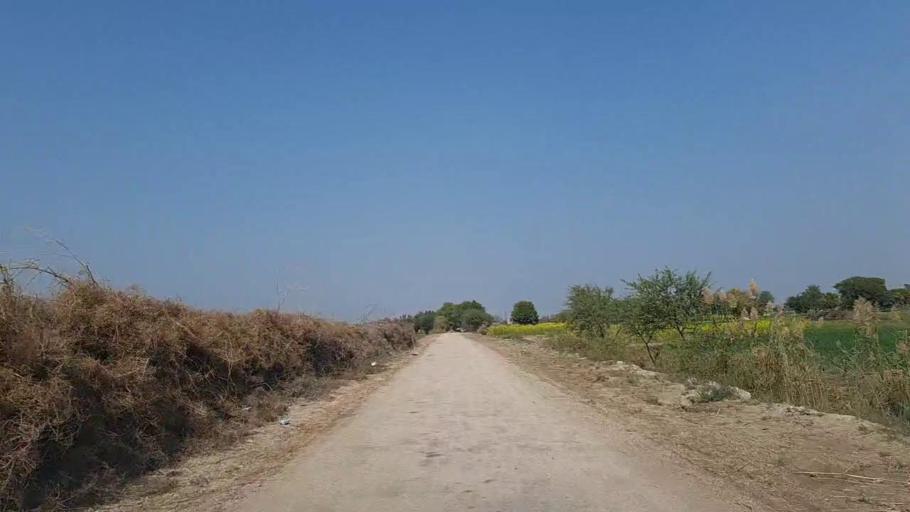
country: PK
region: Sindh
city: Nawabshah
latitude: 26.2889
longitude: 68.5138
